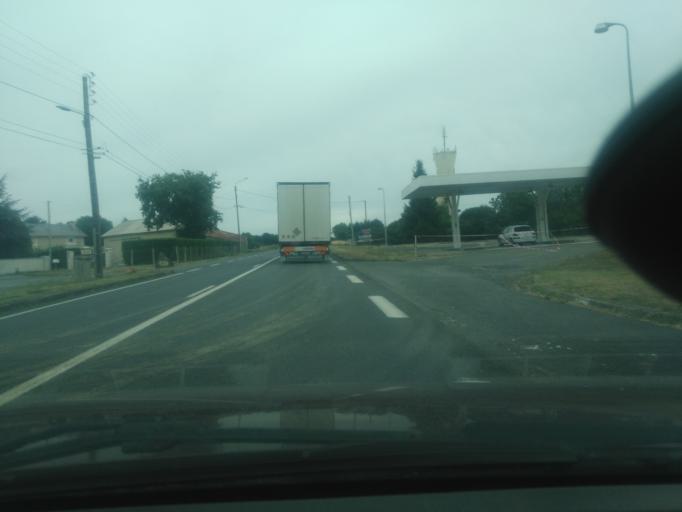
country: FR
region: Poitou-Charentes
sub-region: Departement de la Vienne
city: Sevres-Anxaumont
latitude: 46.5592
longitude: 0.4580
